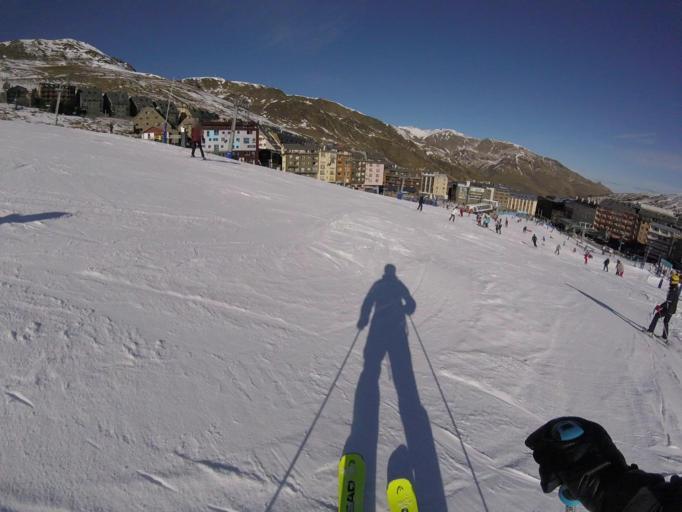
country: AD
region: Encamp
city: Pas de la Casa
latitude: 42.5394
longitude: 1.7323
